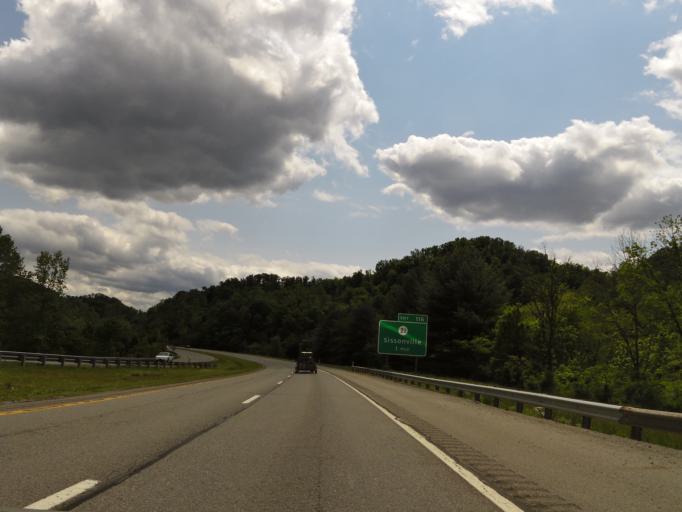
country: US
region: West Virginia
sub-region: Kanawha County
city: Sissonville
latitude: 38.5617
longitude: -81.6365
